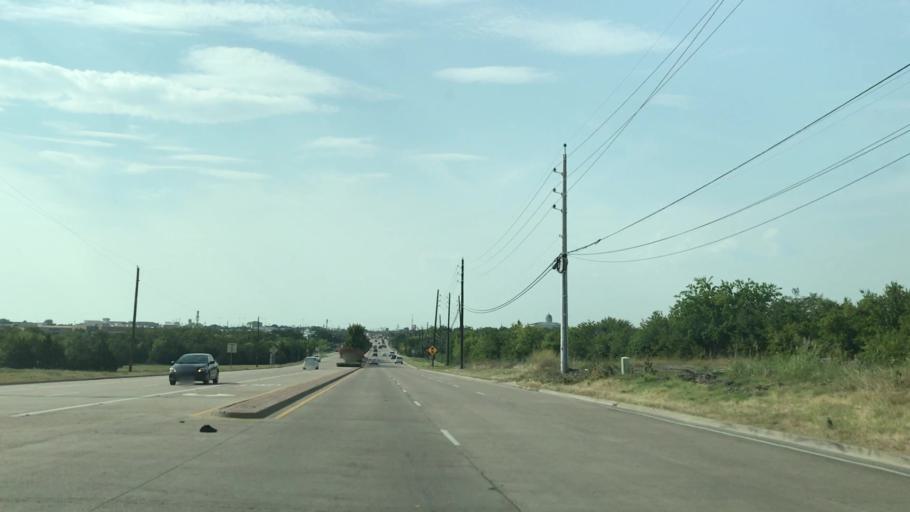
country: US
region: Texas
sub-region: Rockwall County
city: Rockwall
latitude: 32.8997
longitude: -96.4435
